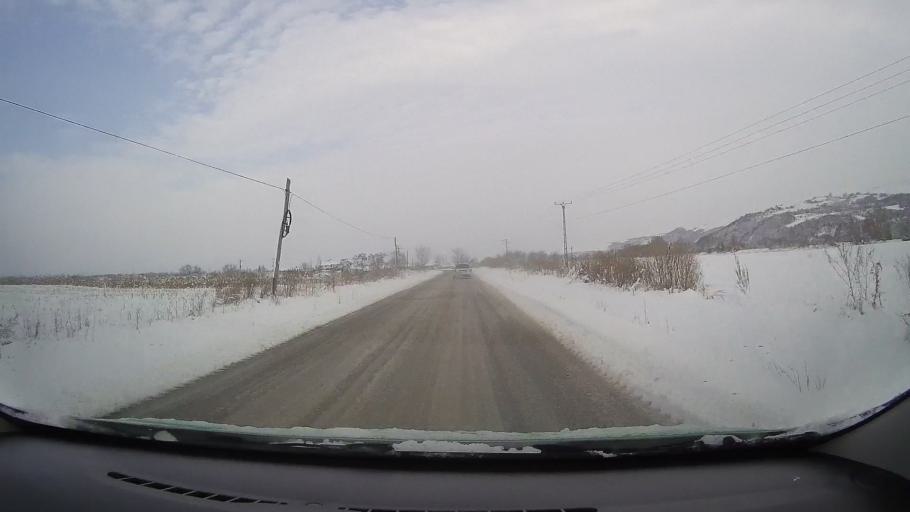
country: RO
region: Alba
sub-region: Comuna Pianu
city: Pianu de Jos
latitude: 45.9205
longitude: 23.4860
